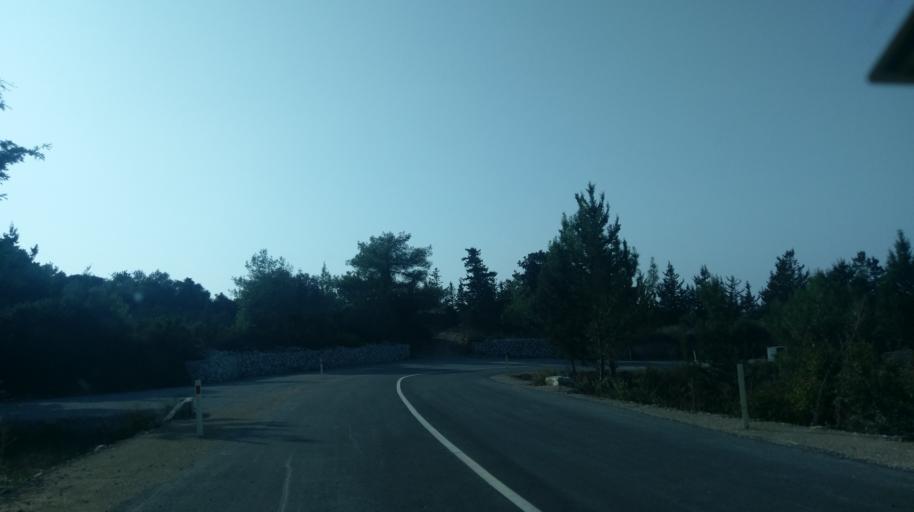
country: CY
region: Ammochostos
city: Leonarisso
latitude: 35.5353
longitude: 34.2330
